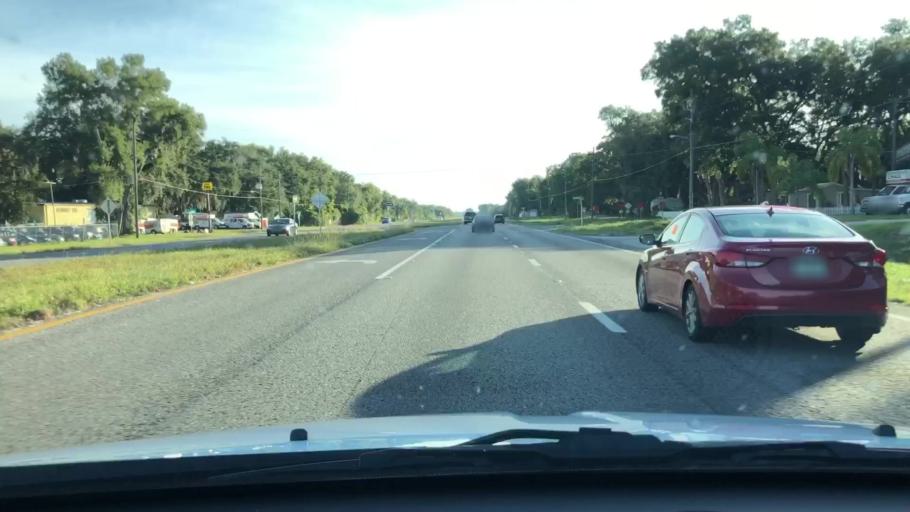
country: US
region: Florida
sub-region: Osceola County
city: Campbell
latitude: 28.2570
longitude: -81.4580
